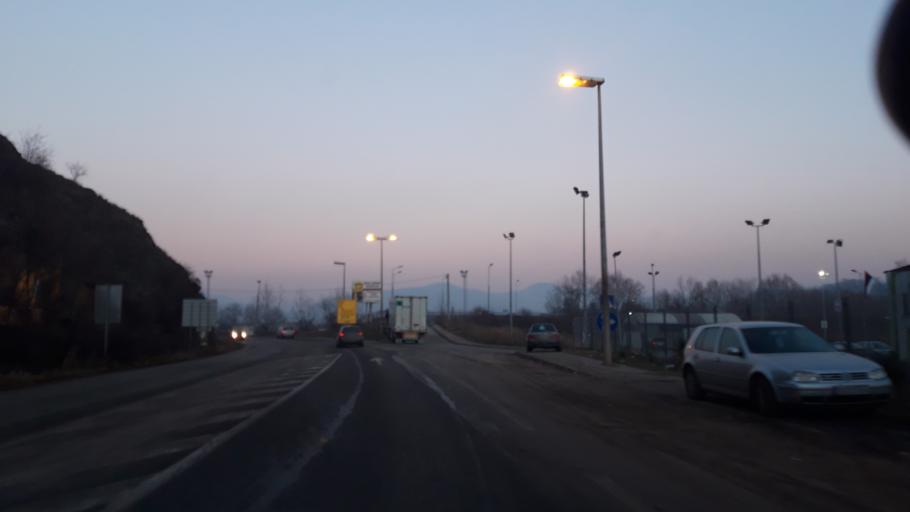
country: BA
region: Republika Srpska
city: Zvornik
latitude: 44.4063
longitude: 19.1219
